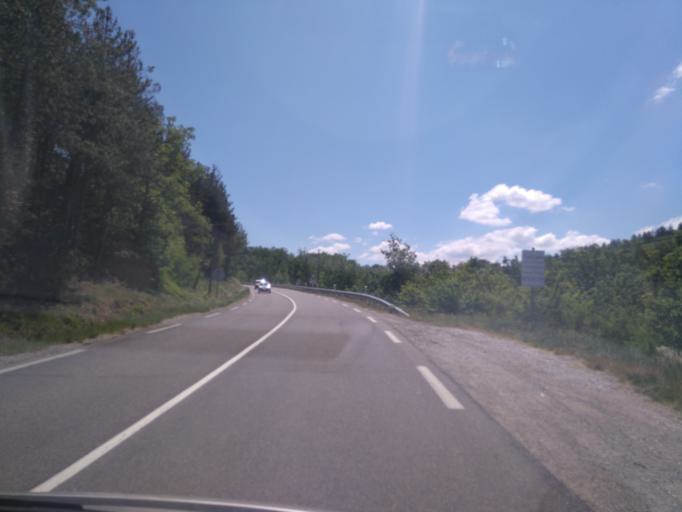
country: FR
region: Provence-Alpes-Cote d'Azur
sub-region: Departement des Hautes-Alpes
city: Laragne-Monteglin
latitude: 44.2866
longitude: 5.8442
